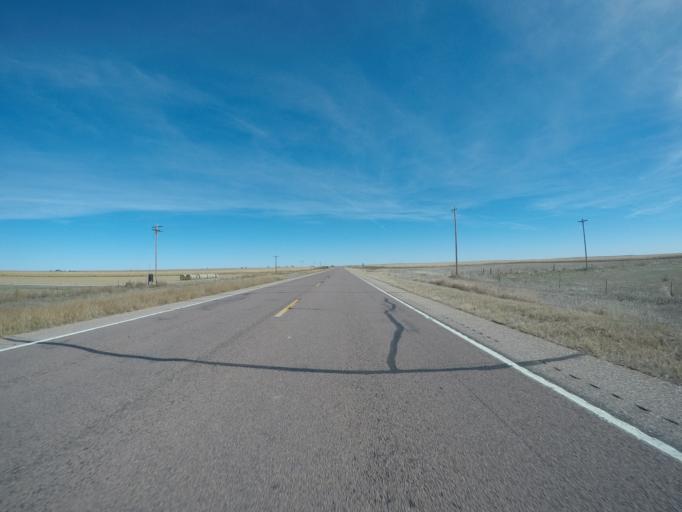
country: US
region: Colorado
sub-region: Kit Carson County
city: Burlington
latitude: 39.6580
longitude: -102.5277
